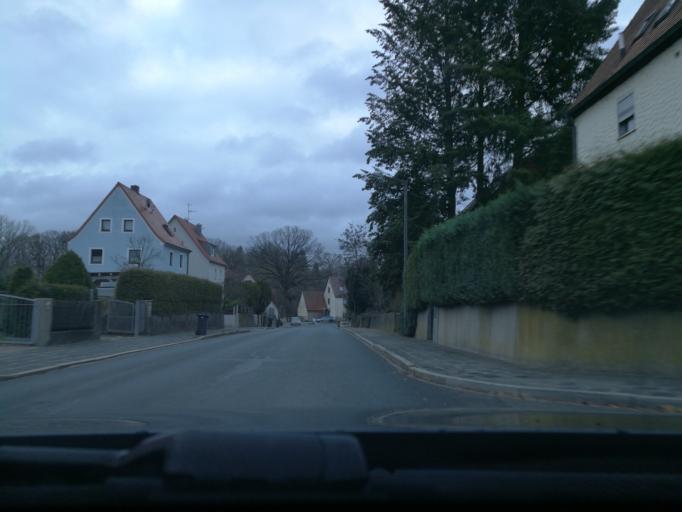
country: DE
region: Bavaria
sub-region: Regierungsbezirk Mittelfranken
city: Heroldsberg
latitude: 49.5397
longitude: 11.1547
